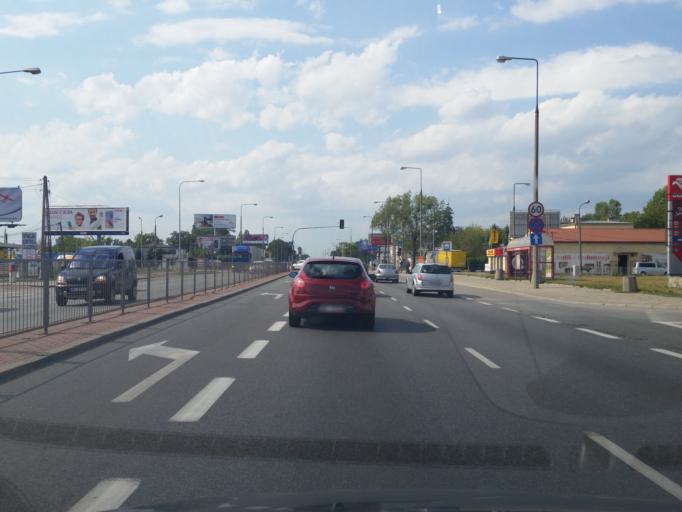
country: PL
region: Masovian Voivodeship
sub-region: Warszawa
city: Wlochy
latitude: 52.1919
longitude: 20.9501
